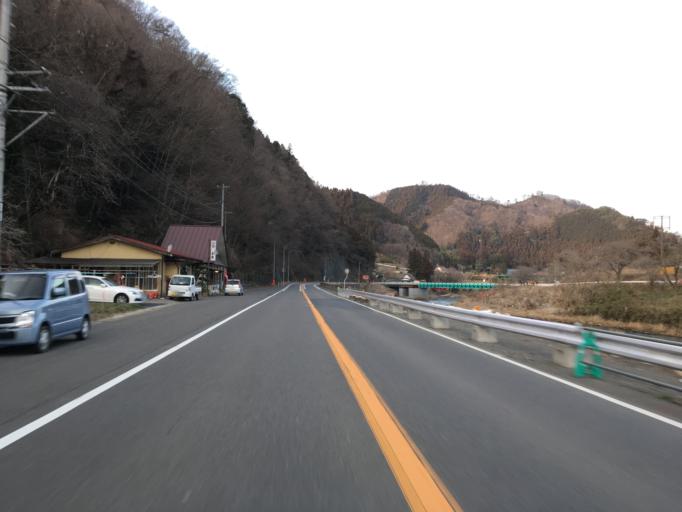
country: JP
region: Ibaraki
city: Daigo
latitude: 36.8418
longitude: 140.3848
